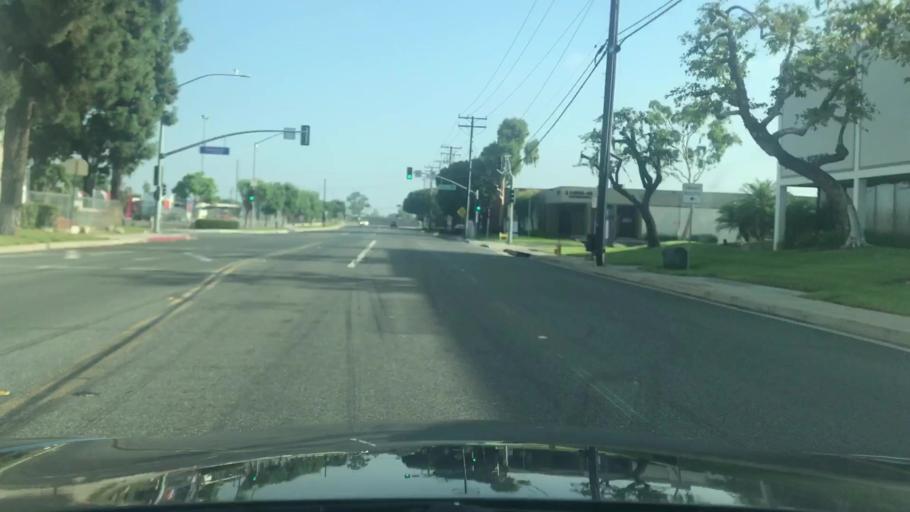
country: US
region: California
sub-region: Los Angeles County
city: Norwalk
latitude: 33.8944
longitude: -118.0554
